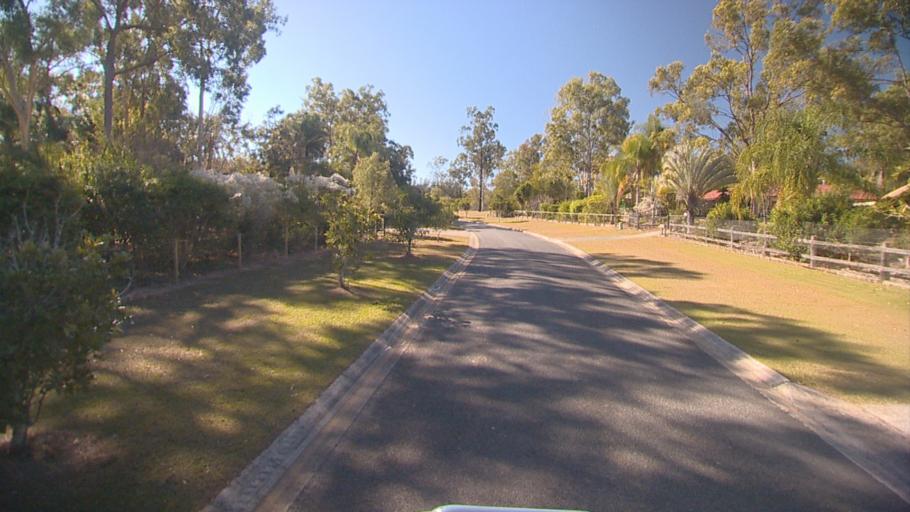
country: AU
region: Queensland
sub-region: Logan
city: North Maclean
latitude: -27.8253
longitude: 152.9412
